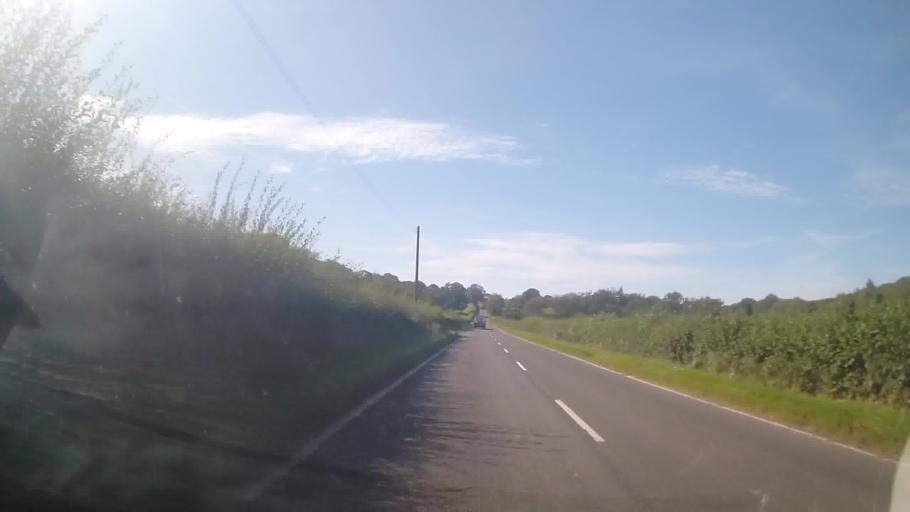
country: GB
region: Wales
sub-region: Sir Powys
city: Llandrindod Wells
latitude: 52.2816
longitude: -3.3720
